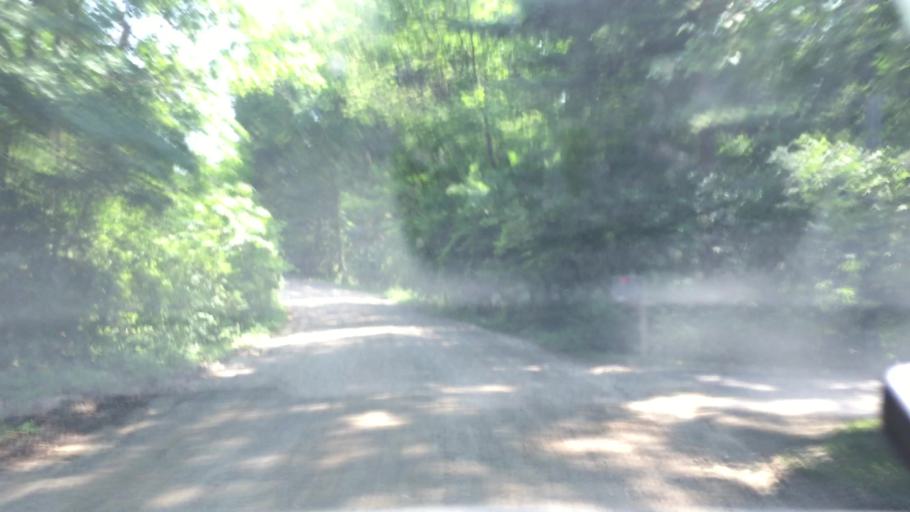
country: US
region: Michigan
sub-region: Oakland County
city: Orchard Lake
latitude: 42.5510
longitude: -83.3347
